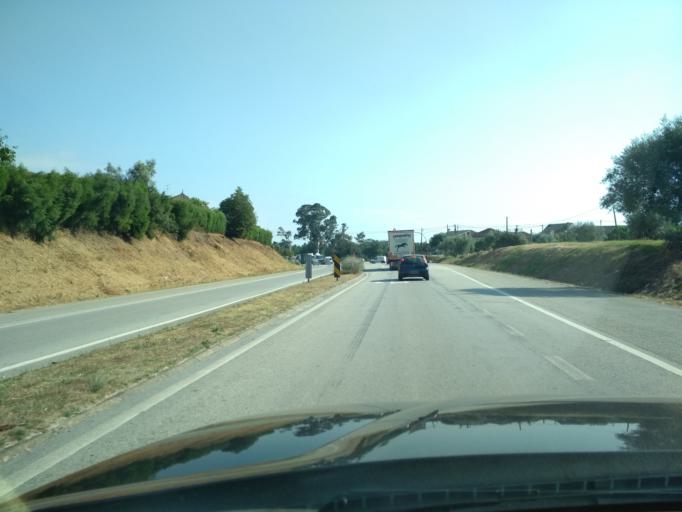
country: PT
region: Aveiro
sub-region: Mealhada
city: Pampilhosa do Botao
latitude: 40.3245
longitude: -8.4543
